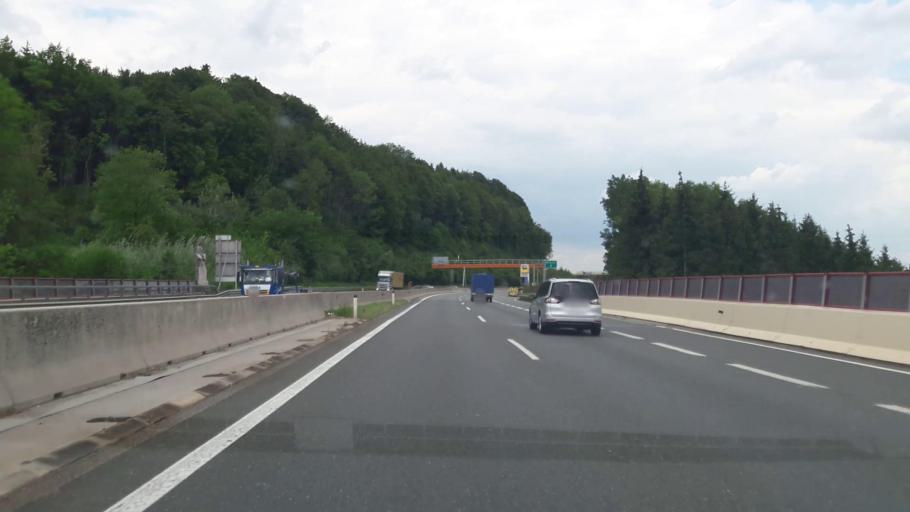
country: AT
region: Salzburg
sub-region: Politischer Bezirk Salzburg-Umgebung
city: Hallwang
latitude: 47.8368
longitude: 13.0743
